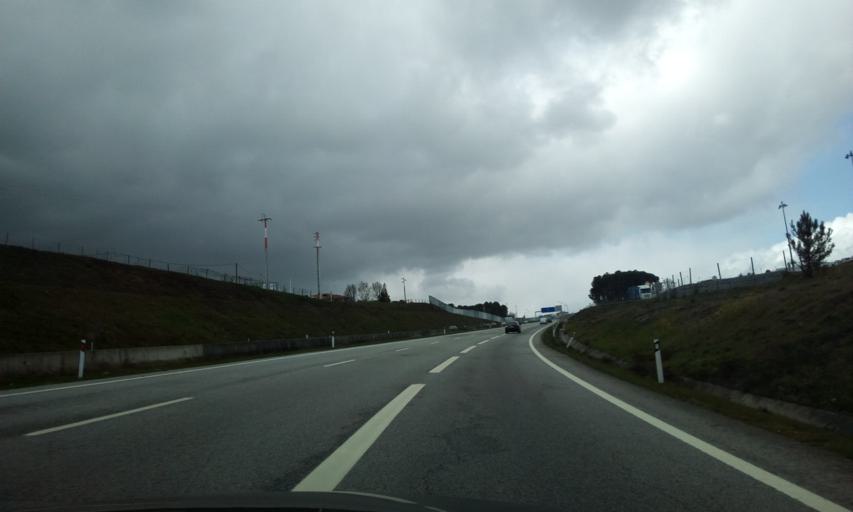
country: PT
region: Viseu
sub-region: Viseu
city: Rio de Loba
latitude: 40.6326
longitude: -7.8439
